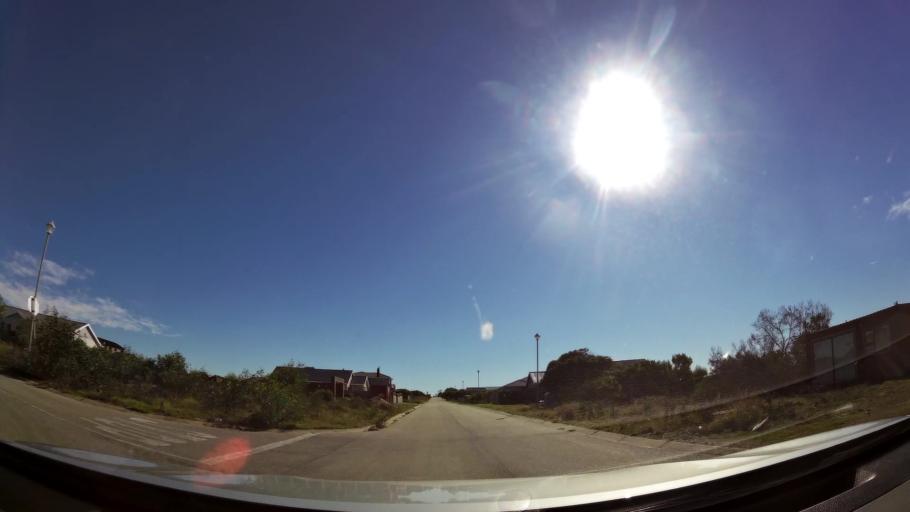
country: ZA
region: Eastern Cape
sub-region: Cacadu District Municipality
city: Jeffrey's Bay
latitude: -34.0375
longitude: 24.9081
